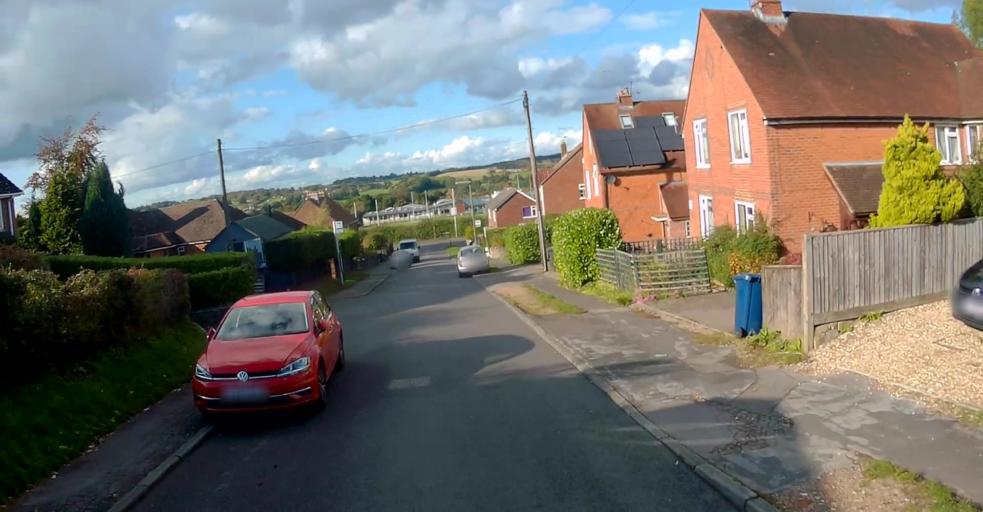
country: GB
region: England
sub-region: Surrey
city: Farnham
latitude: 51.1987
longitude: -0.8124
